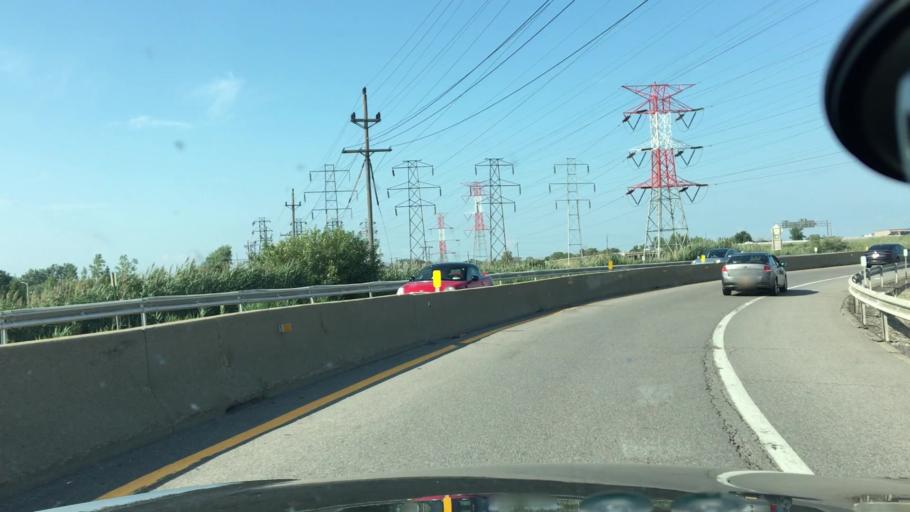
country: US
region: New York
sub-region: Erie County
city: Cheektowaga
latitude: 42.9110
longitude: -78.7692
